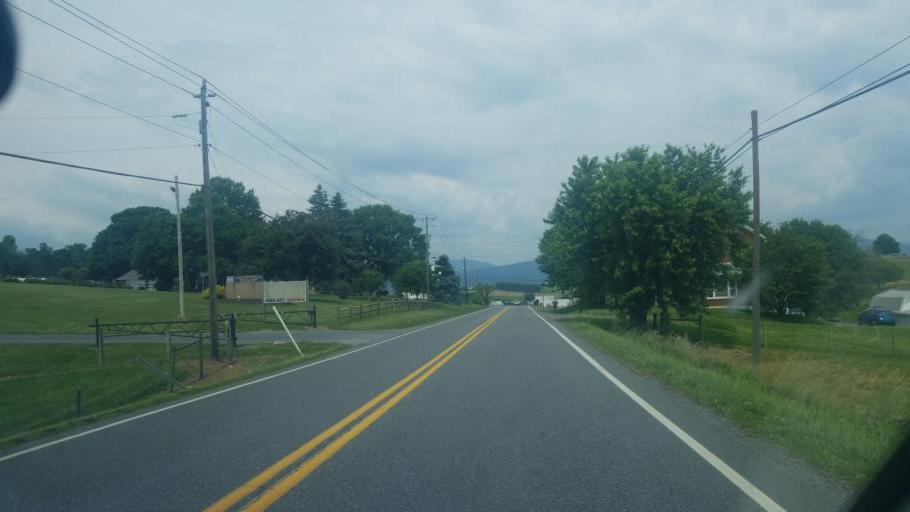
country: US
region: Virginia
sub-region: Rockingham County
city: Dayton
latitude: 38.4622
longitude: -78.9613
